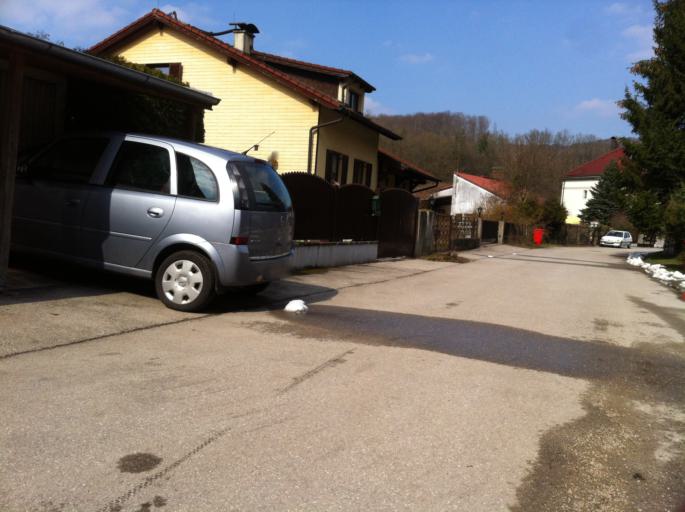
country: AT
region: Lower Austria
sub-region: Politischer Bezirk Wien-Umgebung
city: Purkersdorf
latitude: 48.1952
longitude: 16.1452
